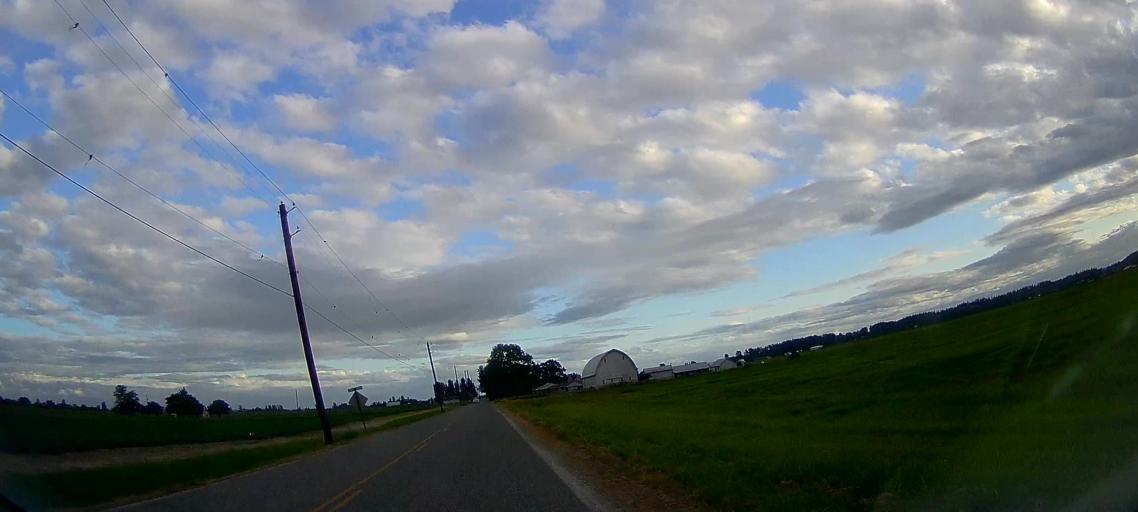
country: US
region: Washington
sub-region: Skagit County
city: Mount Vernon
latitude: 48.3835
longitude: -122.3999
